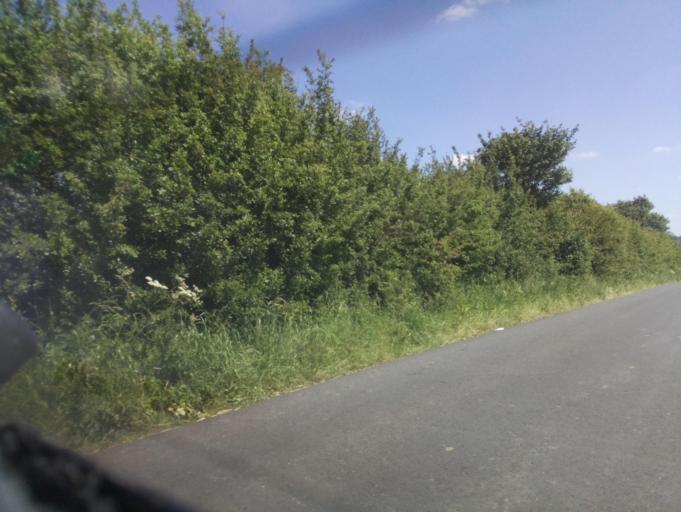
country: GB
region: England
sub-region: Wiltshire
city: Royal Wootton Bassett
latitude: 51.5164
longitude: -1.8972
